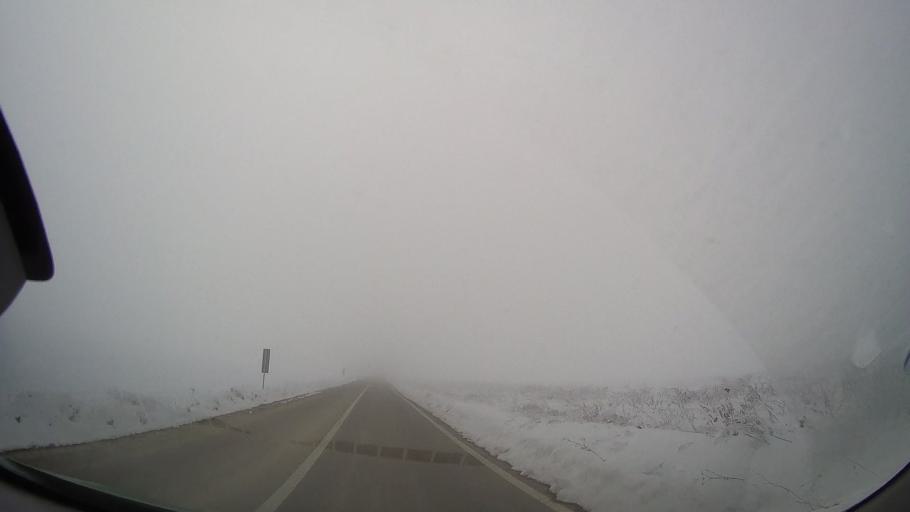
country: RO
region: Iasi
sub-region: Comuna Valea Seaca
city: Topile
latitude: 47.2754
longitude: 26.6709
